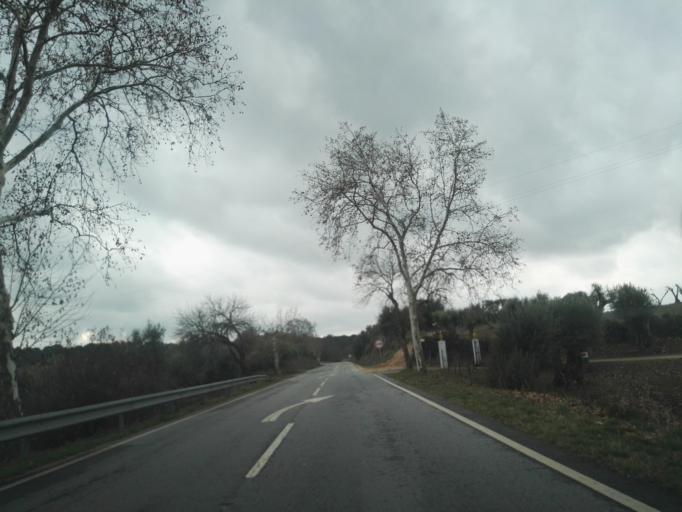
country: PT
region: Portalegre
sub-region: Arronches
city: Arronches
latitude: 39.1298
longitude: -7.2939
